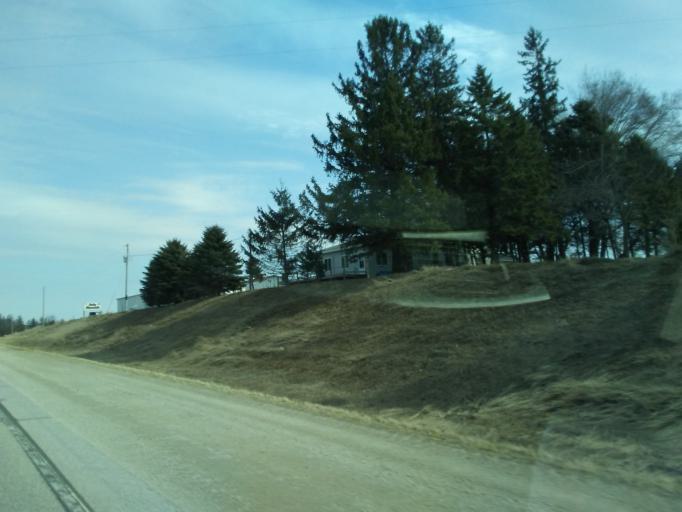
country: US
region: Iowa
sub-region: Allamakee County
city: Waukon
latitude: 43.2404
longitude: -91.5061
